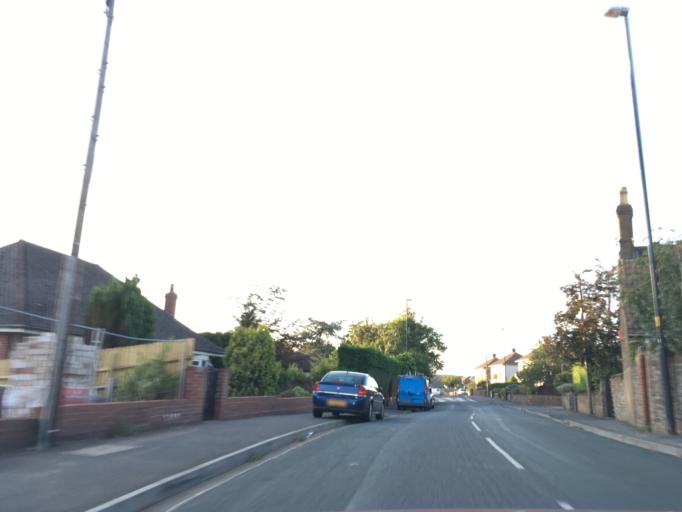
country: GB
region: England
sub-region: South Gloucestershire
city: Kingswood
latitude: 51.4460
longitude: -2.5414
